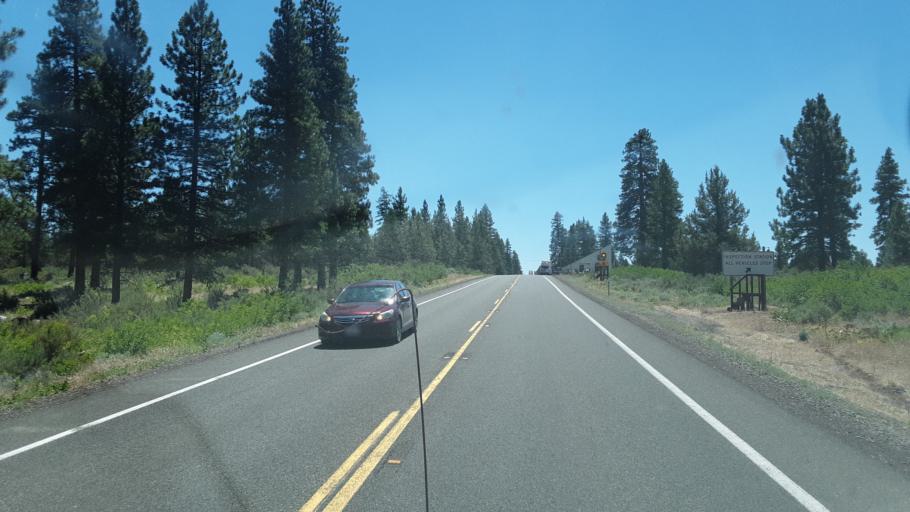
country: US
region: California
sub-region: Siskiyou County
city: Tulelake
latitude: 41.6134
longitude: -121.2140
